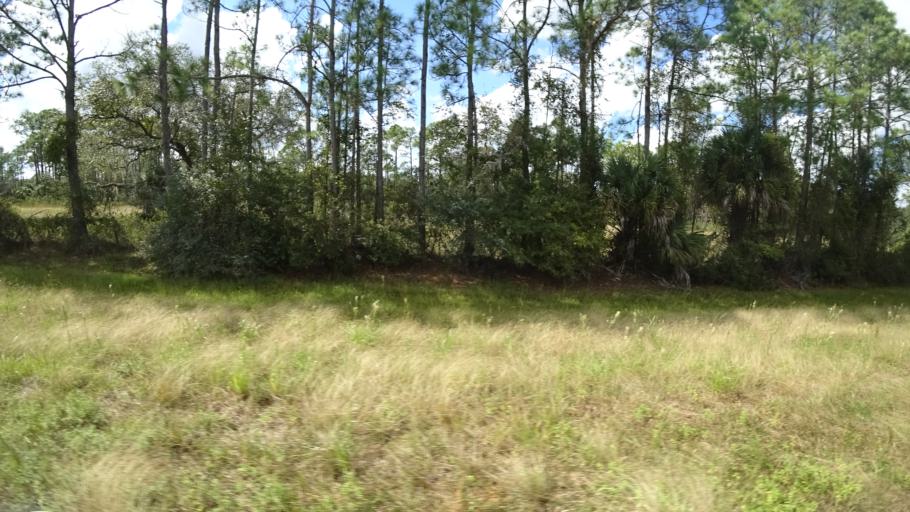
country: US
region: Florida
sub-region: Sarasota County
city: North Port
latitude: 27.2464
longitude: -82.1219
